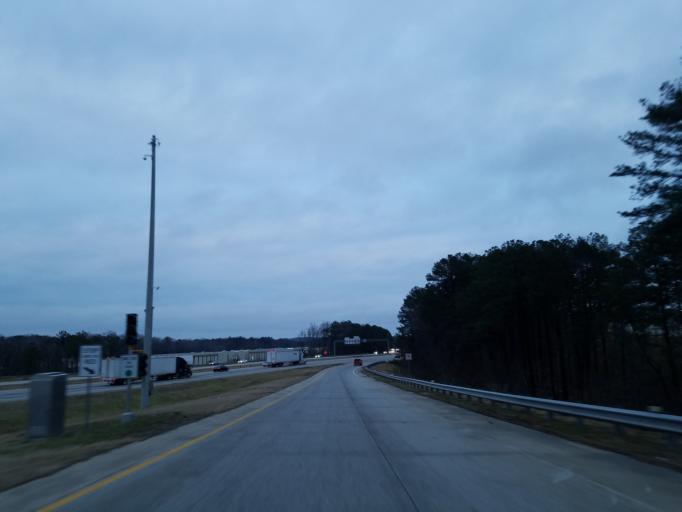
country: US
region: Georgia
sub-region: Cobb County
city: Acworth
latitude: 34.0785
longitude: -84.6518
